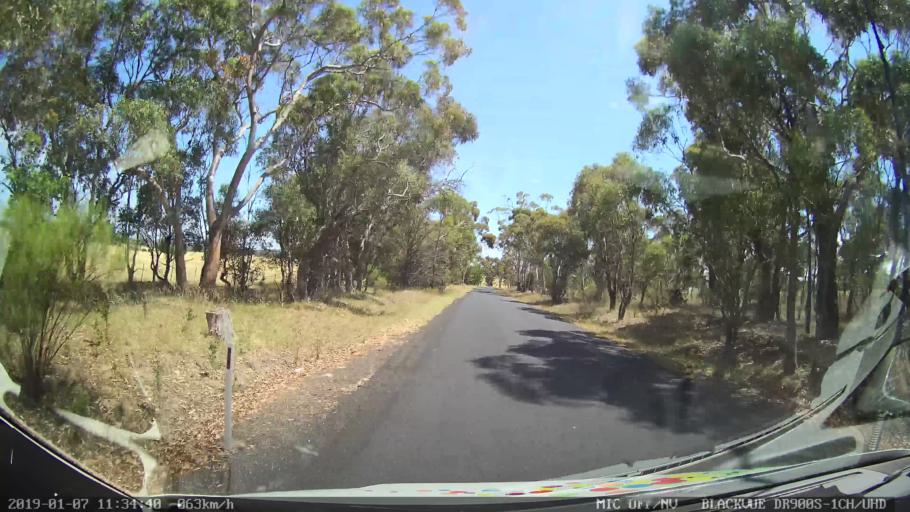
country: AU
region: New South Wales
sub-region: Armidale Dumaresq
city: Armidale
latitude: -30.3878
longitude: 151.5579
